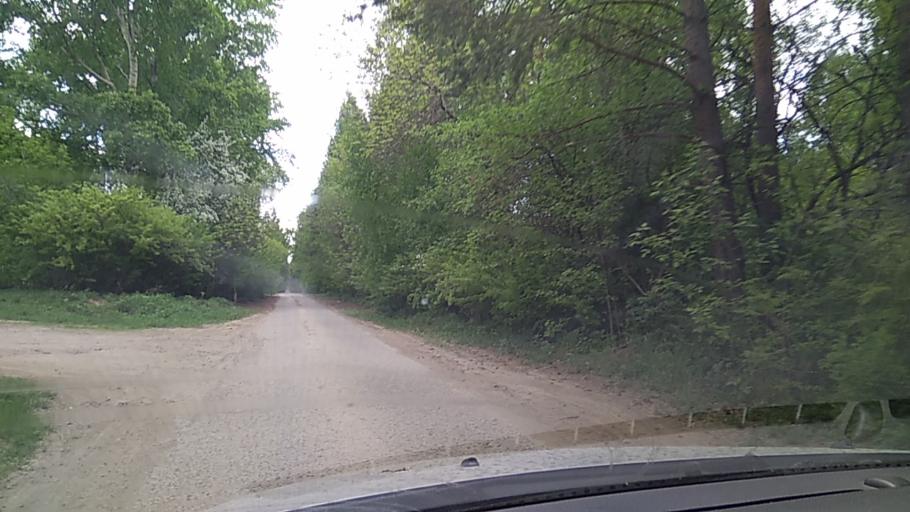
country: RU
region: Sverdlovsk
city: Verkhnyaya Pyshma
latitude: 56.9243
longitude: 60.6020
